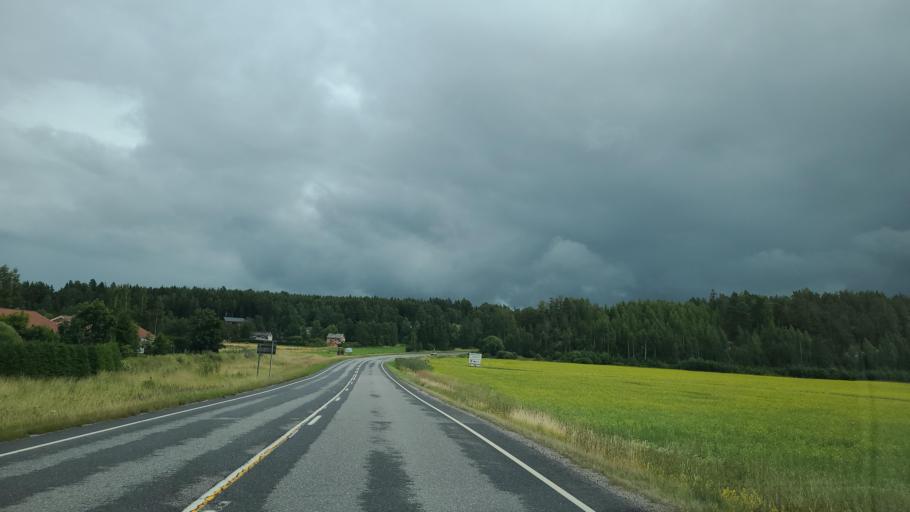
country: FI
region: Varsinais-Suomi
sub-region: Turku
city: Sauvo
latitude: 60.3406
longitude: 22.6938
